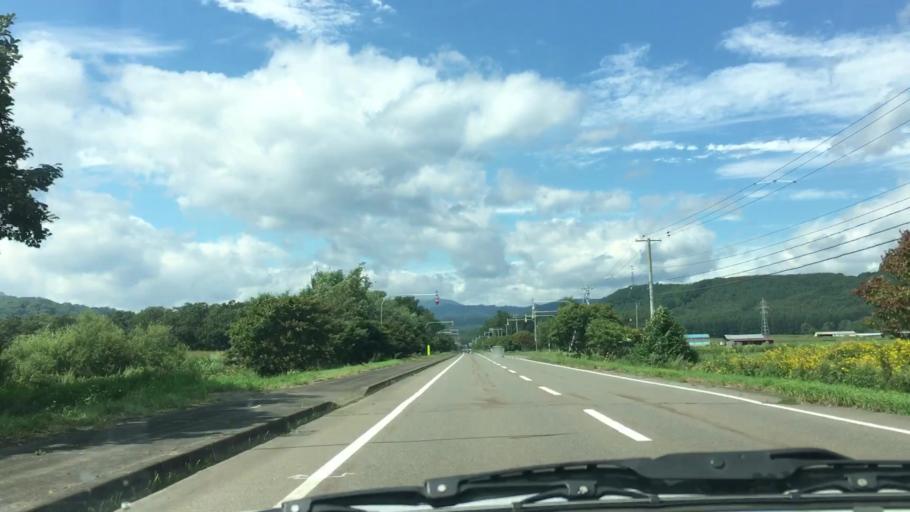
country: JP
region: Hokkaido
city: Otofuke
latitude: 43.3132
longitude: 143.3067
